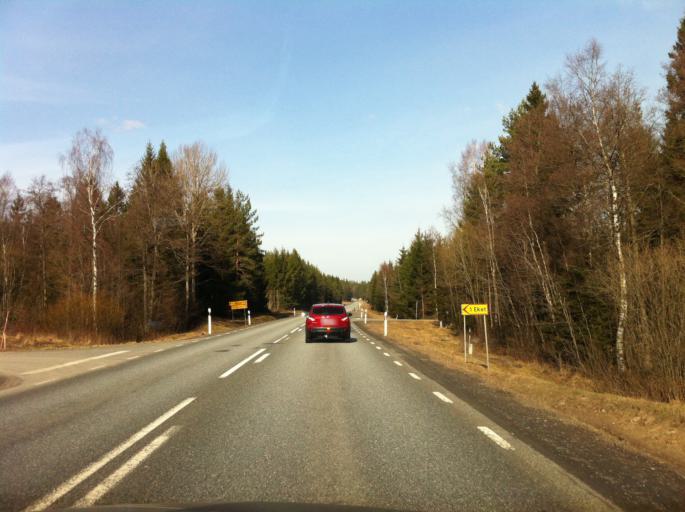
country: SE
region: Joenkoeping
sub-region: Mullsjo Kommun
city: Mullsjoe
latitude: 57.9996
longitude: 13.8300
